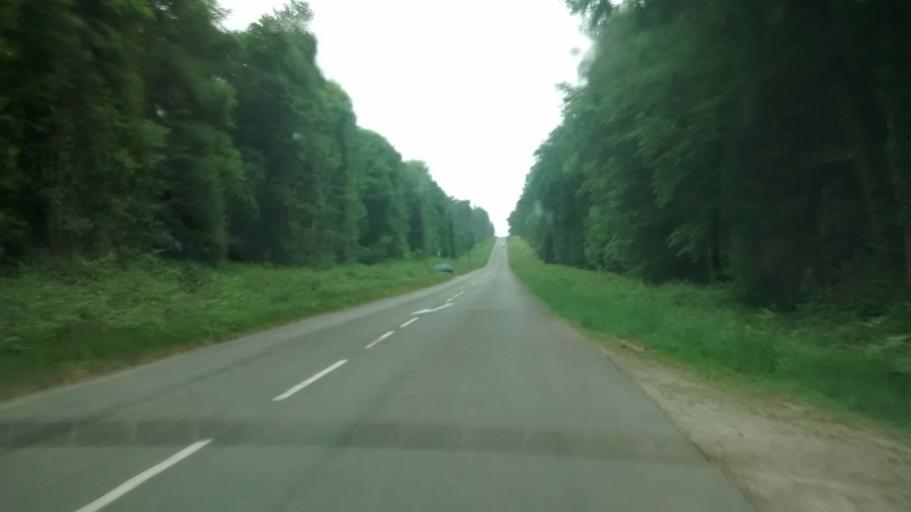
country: FR
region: Brittany
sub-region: Departement d'Ille-et-Vilaine
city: Paimpont
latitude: 48.0077
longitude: -2.2092
